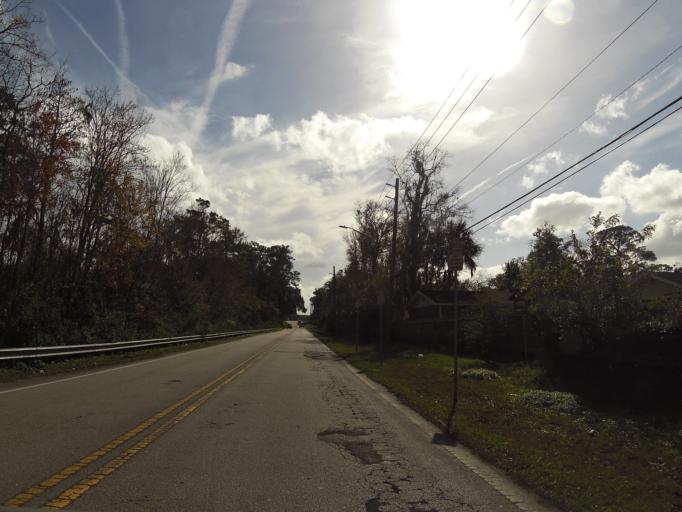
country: US
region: Florida
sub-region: Duval County
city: Jacksonville
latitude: 30.3341
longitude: -81.5603
